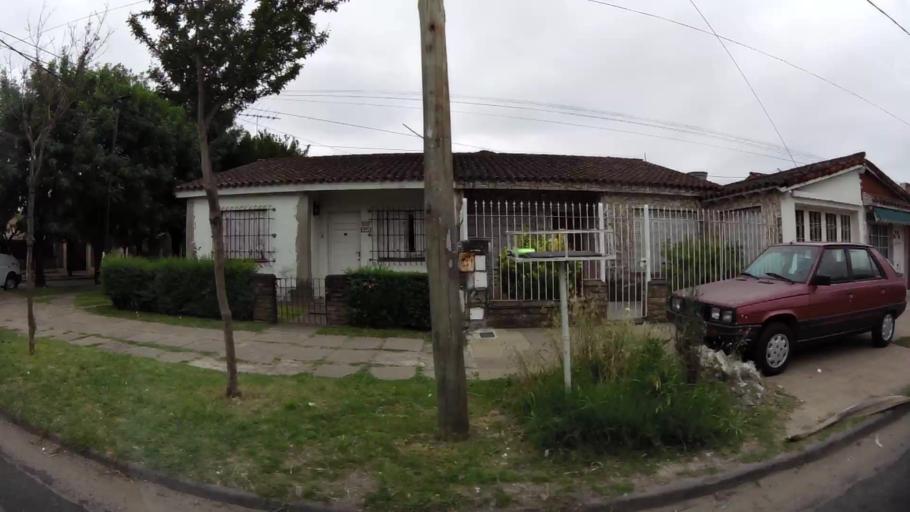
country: AR
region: Buenos Aires
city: San Justo
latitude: -34.7149
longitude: -58.5418
